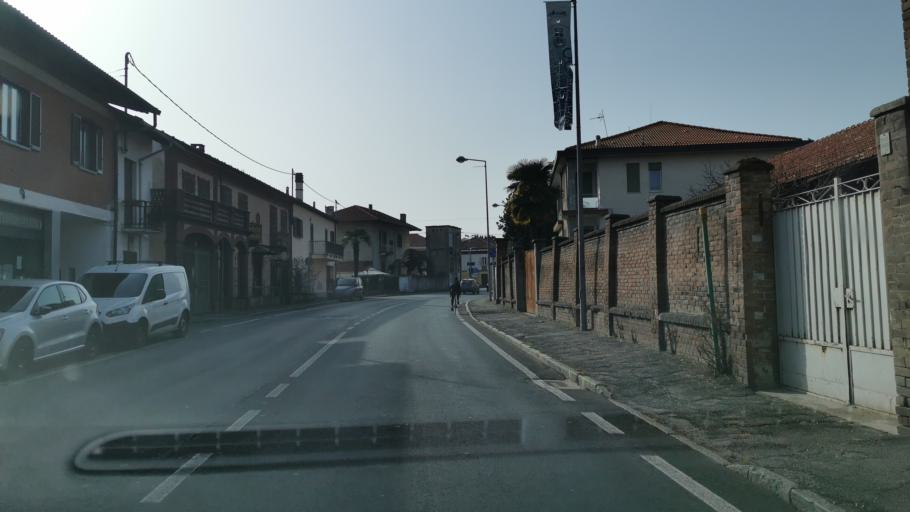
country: IT
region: Piedmont
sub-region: Provincia di Torino
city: Volpiano
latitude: 45.1996
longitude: 7.7763
